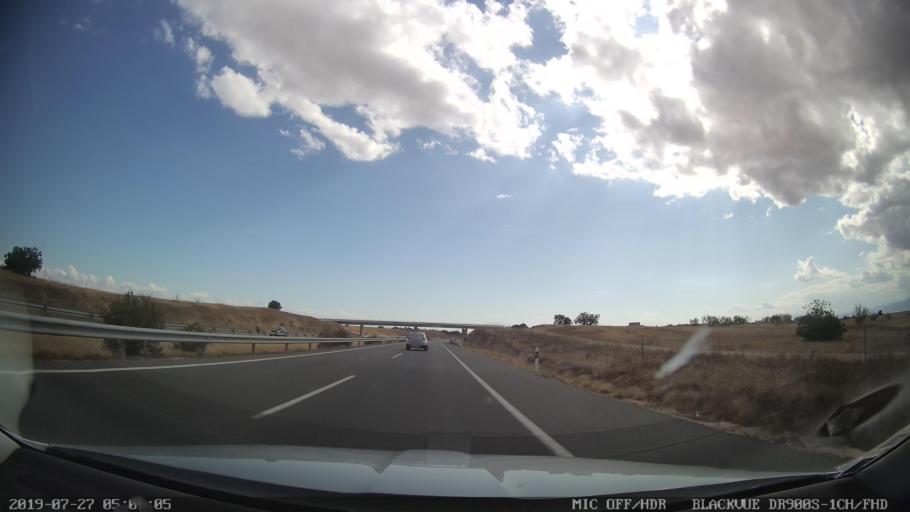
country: ES
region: Castille-La Mancha
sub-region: Province of Toledo
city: Santa Cruz del Retamar
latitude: 40.1211
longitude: -4.2583
